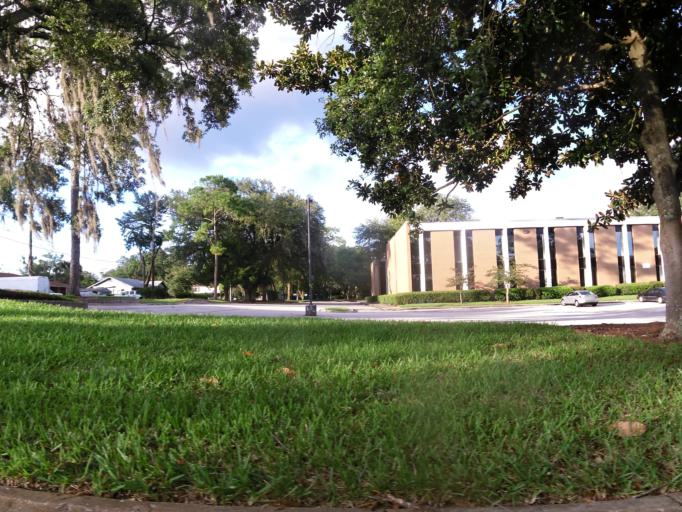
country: US
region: Florida
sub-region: Duval County
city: Jacksonville
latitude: 30.3015
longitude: -81.6166
